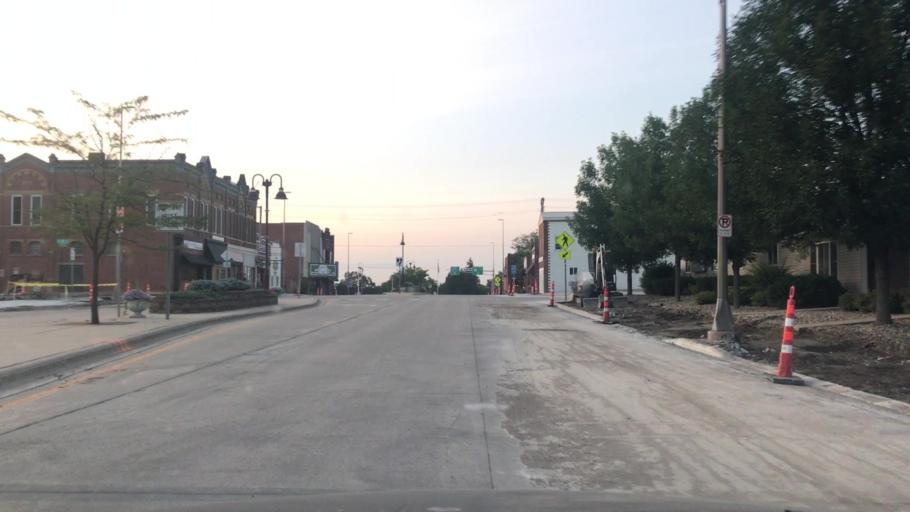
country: US
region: Minnesota
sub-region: Redwood County
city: Redwood Falls
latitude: 44.5390
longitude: -95.1194
